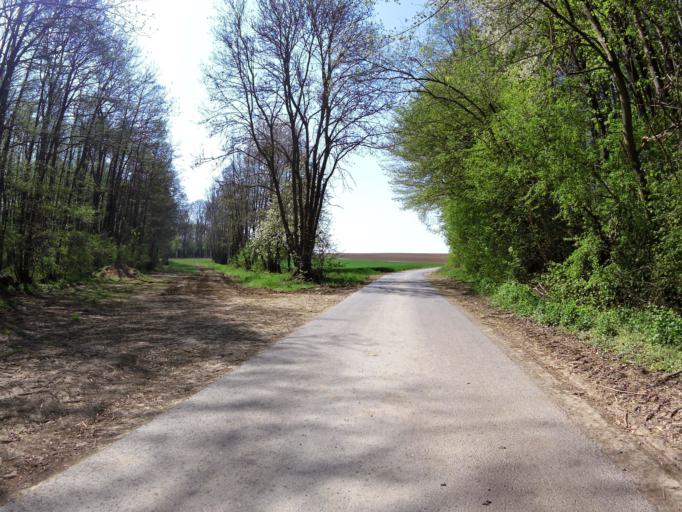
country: DE
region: Bavaria
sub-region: Regierungsbezirk Unterfranken
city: Giebelstadt
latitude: 49.6952
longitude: 9.9633
